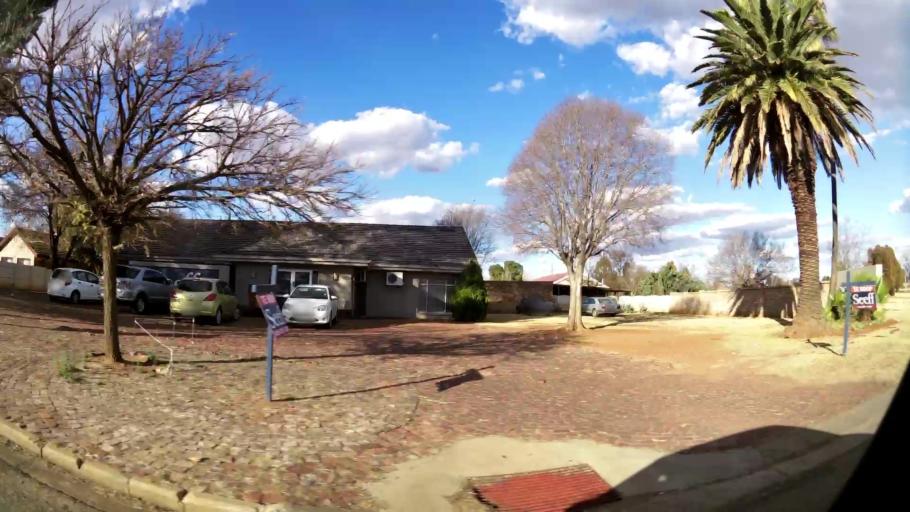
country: ZA
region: North-West
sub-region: Dr Kenneth Kaunda District Municipality
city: Potchefstroom
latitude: -26.6998
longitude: 27.0983
